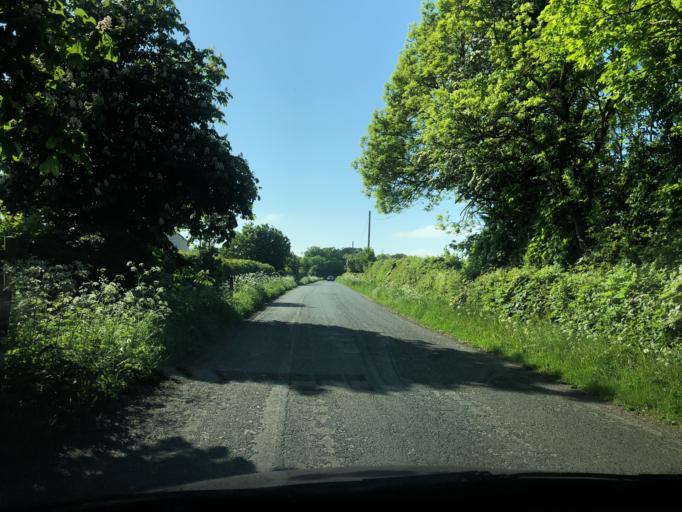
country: GB
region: England
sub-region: North Yorkshire
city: Northallerton
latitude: 54.3211
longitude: -1.3867
